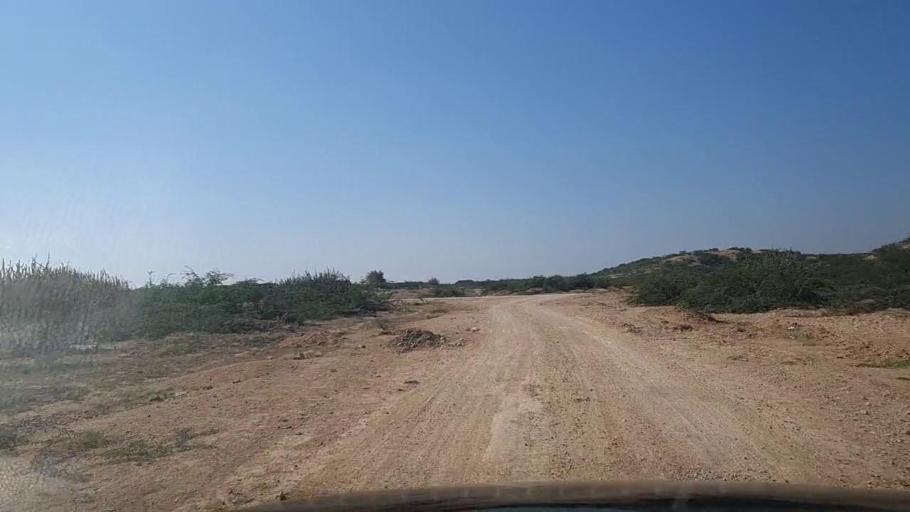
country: PK
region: Sindh
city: Thatta
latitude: 24.6209
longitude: 67.8427
